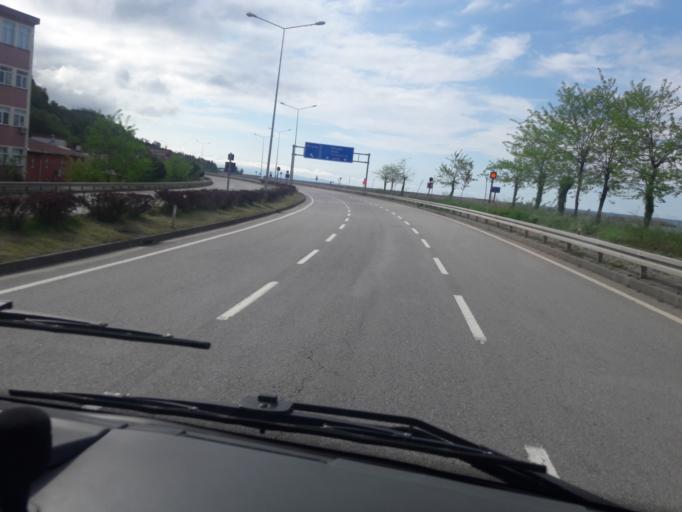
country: TR
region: Giresun
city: Piraziz
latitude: 40.9570
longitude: 38.1182
